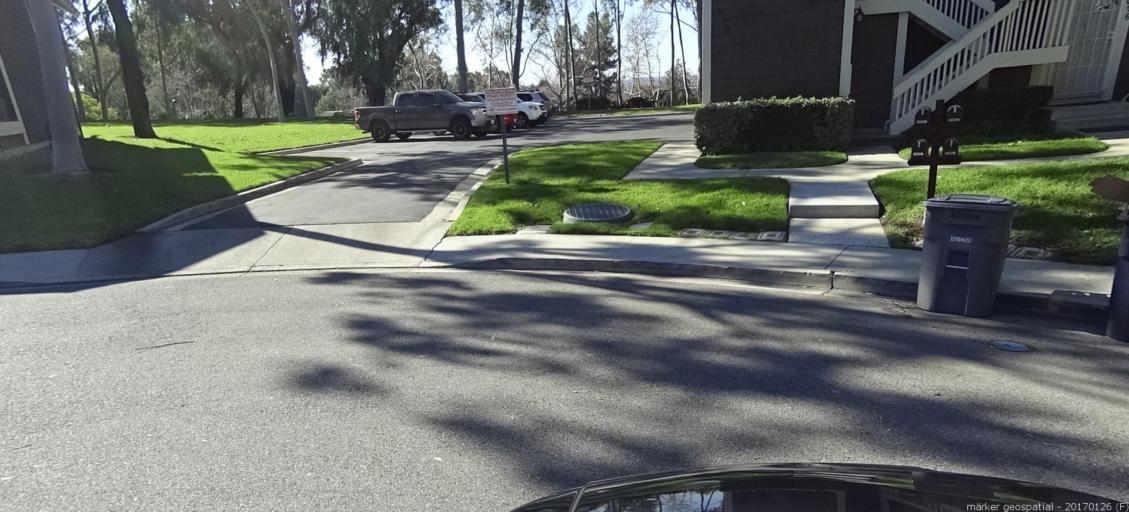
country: US
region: California
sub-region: Orange County
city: Lake Forest
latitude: 33.6379
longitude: -117.6750
